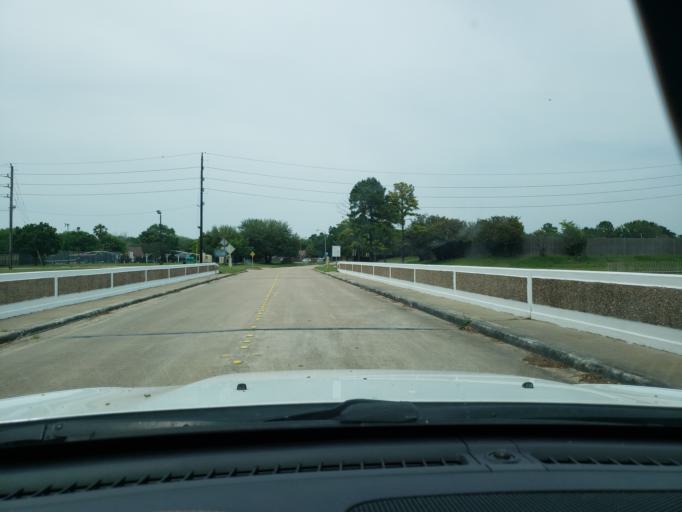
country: US
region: Texas
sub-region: Harris County
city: Jersey Village
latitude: 29.9114
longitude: -95.5735
